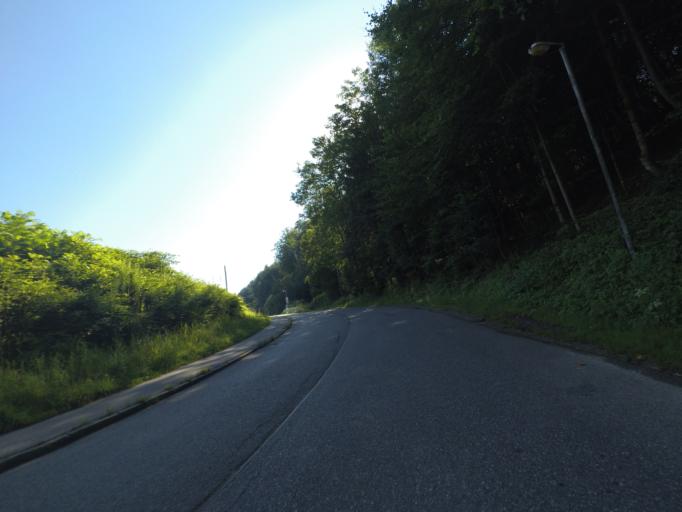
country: AT
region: Salzburg
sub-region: Politischer Bezirk Salzburg-Umgebung
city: Hallwang
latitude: 47.8566
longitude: 13.0883
